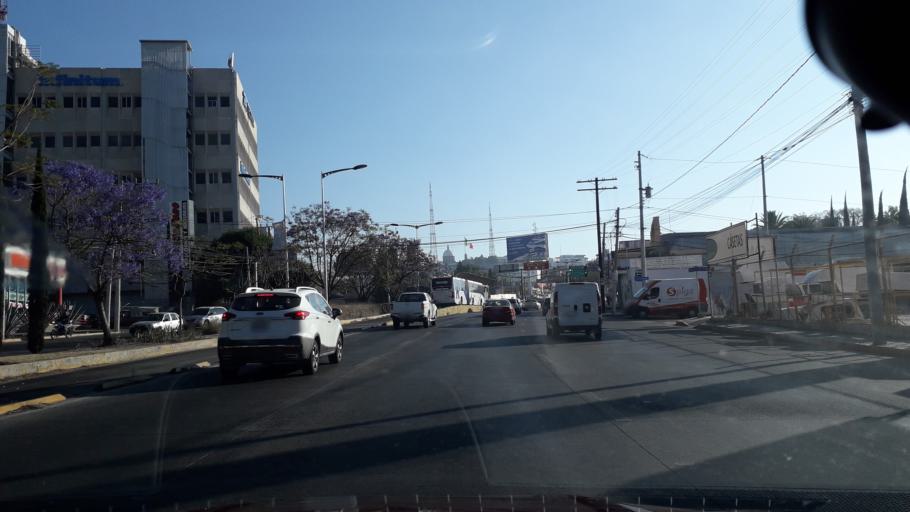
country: MX
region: Puebla
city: Puebla
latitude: 19.0482
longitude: -98.2328
